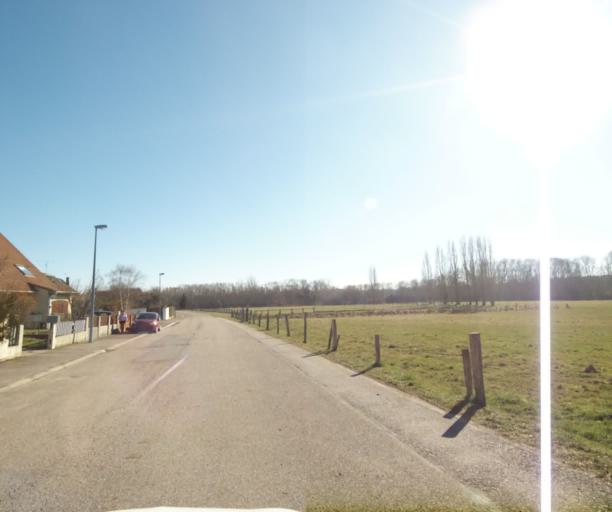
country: FR
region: Lorraine
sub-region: Departement de Meurthe-et-Moselle
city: Tomblaine
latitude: 48.6774
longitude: 6.2147
